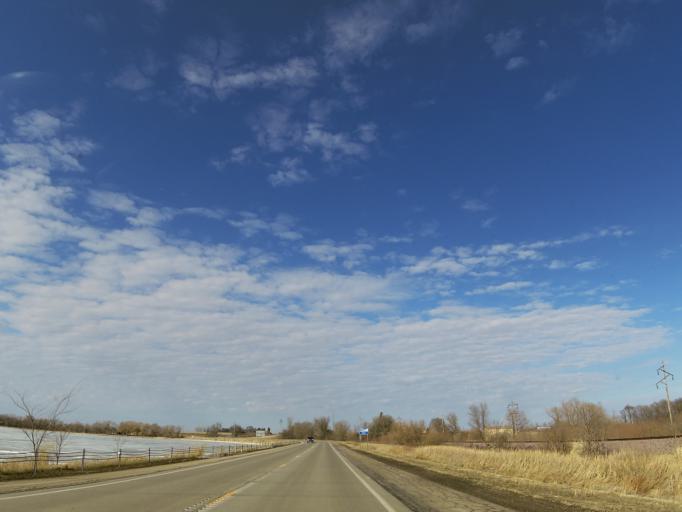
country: US
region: Minnesota
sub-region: Le Sueur County
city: Montgomery
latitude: 44.4748
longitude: -93.5826
